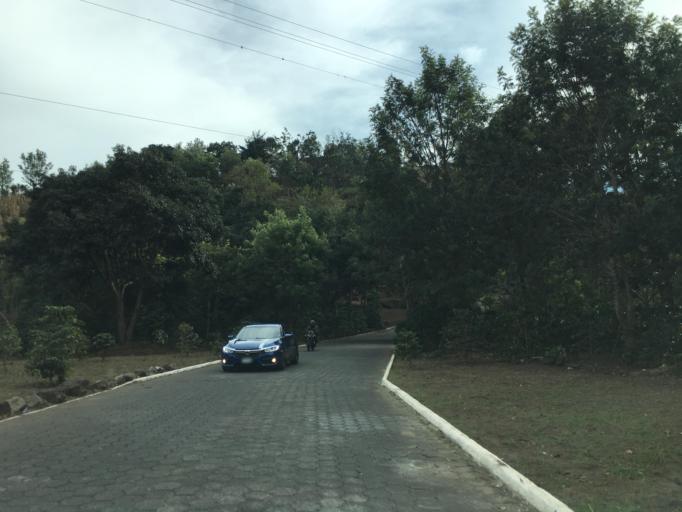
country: GT
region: Solola
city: Santa Catarina Palopo
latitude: 14.6675
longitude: -91.1711
